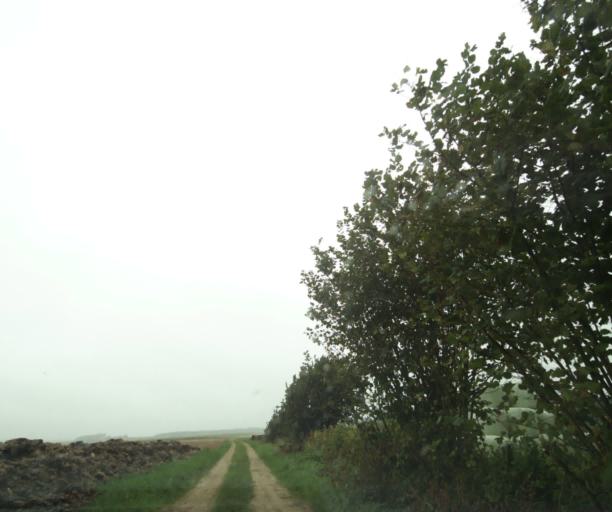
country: FR
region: Nord-Pas-de-Calais
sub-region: Departement du Pas-de-Calais
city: Saint-Josse
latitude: 50.5076
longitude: 1.6726
